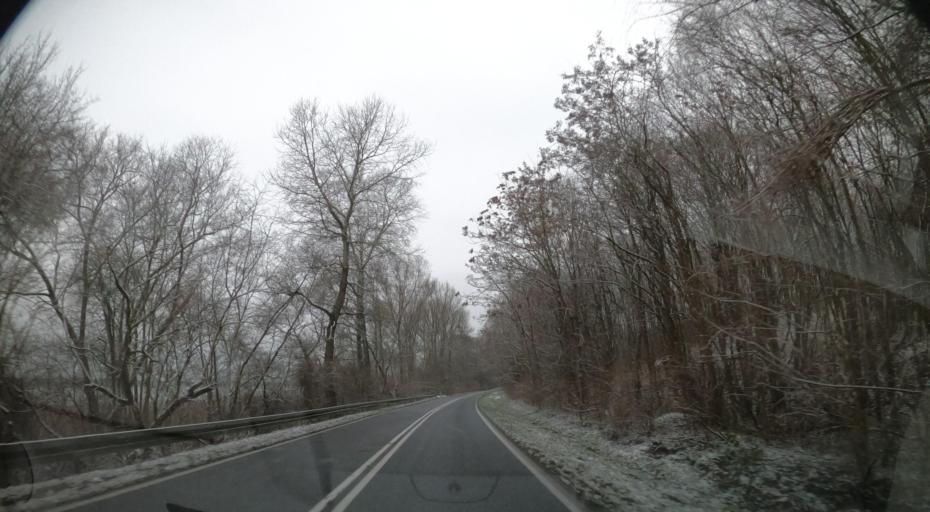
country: PL
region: Masovian Voivodeship
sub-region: Powiat plocki
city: Maszewo Duze
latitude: 52.5707
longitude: 19.5683
